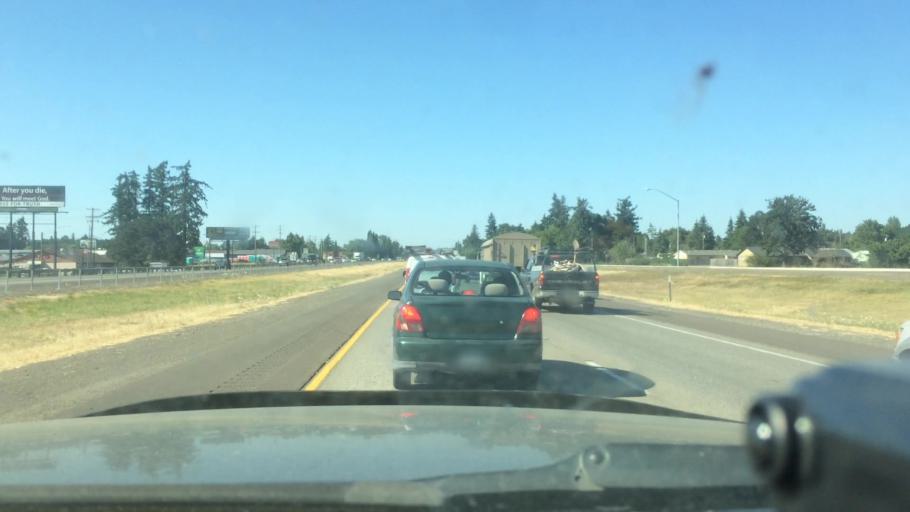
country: US
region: Oregon
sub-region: Linn County
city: Millersburg
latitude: 44.6472
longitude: -123.0622
